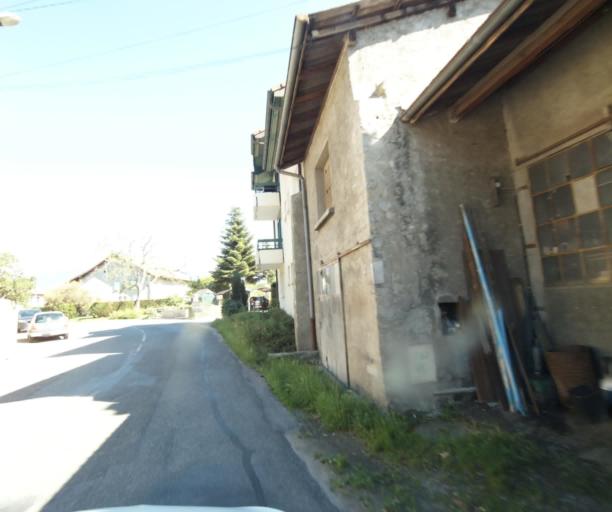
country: FR
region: Rhone-Alpes
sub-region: Departement de la Haute-Savoie
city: Sciez
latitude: 46.3275
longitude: 6.3789
